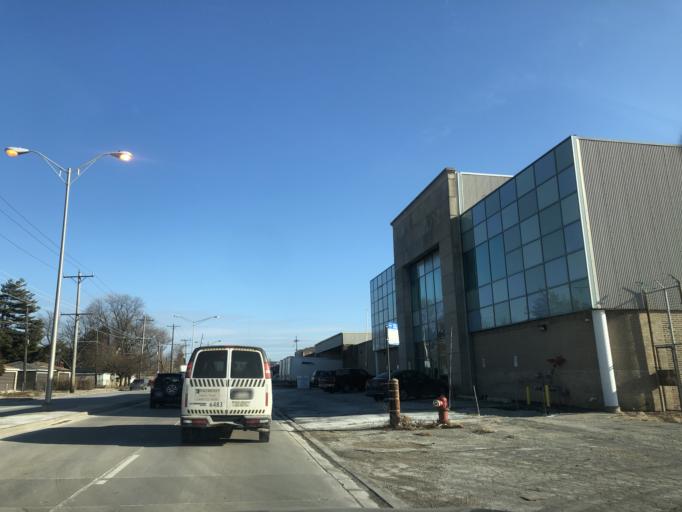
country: US
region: Illinois
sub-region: Cook County
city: Hometown
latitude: 41.7746
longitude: -87.7503
